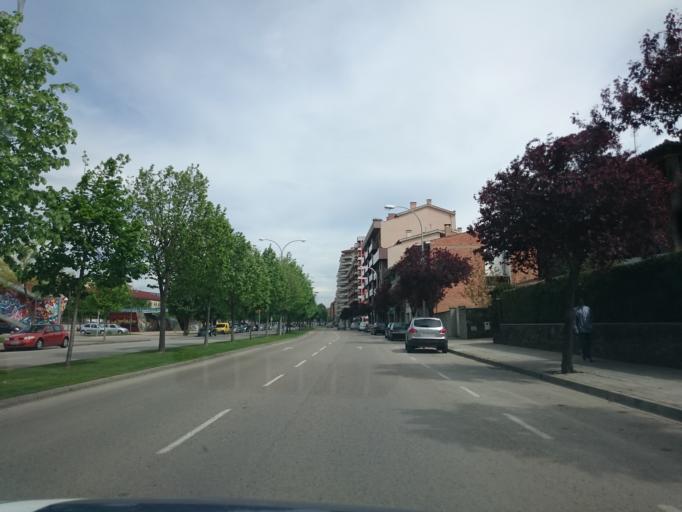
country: ES
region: Catalonia
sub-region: Provincia de Barcelona
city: Vic
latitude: 41.9262
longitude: 2.2490
